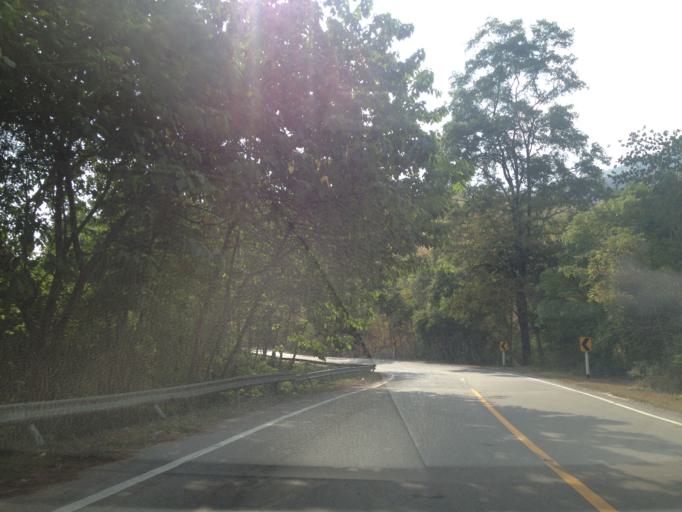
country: TH
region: Chiang Mai
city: Hot
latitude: 18.2303
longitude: 98.5591
